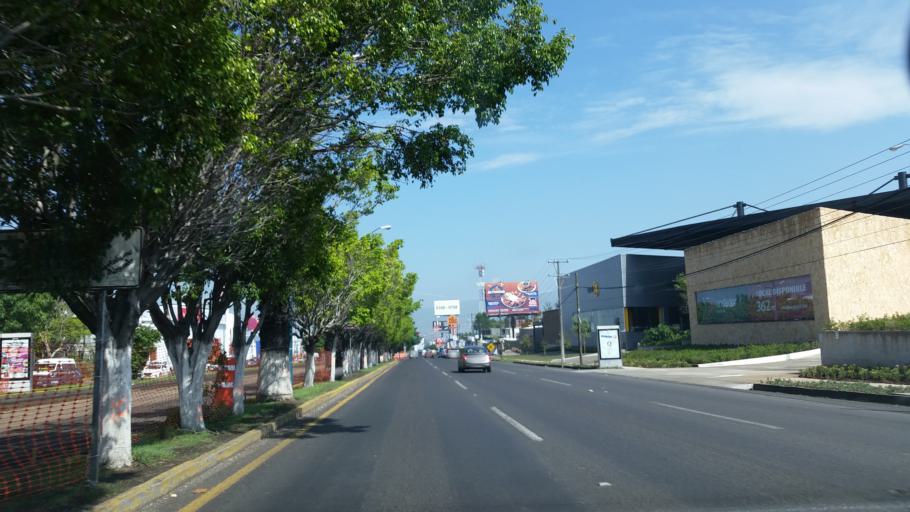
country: MX
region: Michoacan
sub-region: Morelia
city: Morelos
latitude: 19.6735
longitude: -101.2127
